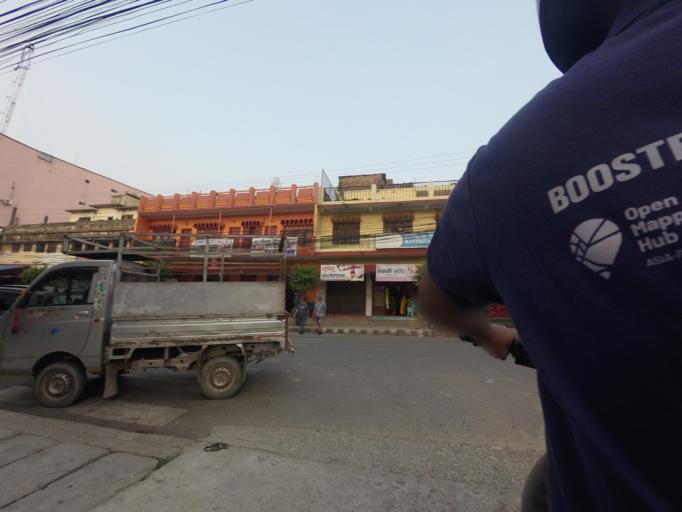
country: NP
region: Western Region
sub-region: Lumbini Zone
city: Bhairahawa
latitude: 27.5092
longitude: 83.4513
